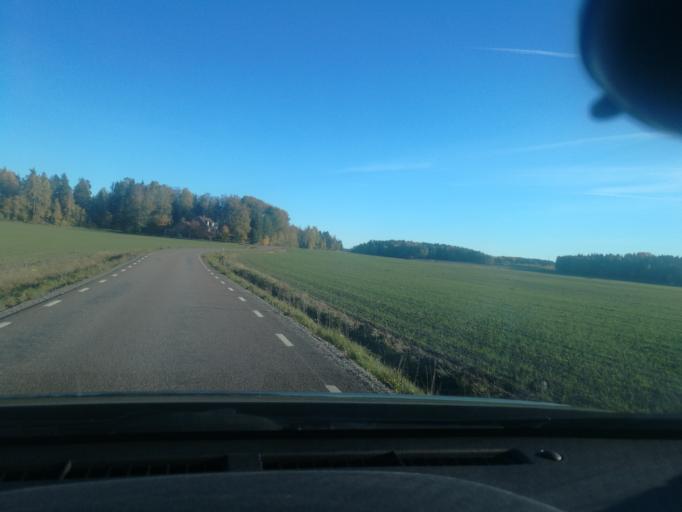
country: SE
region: Vaestmanland
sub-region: Kopings Kommun
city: Koping
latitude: 59.5695
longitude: 16.0266
